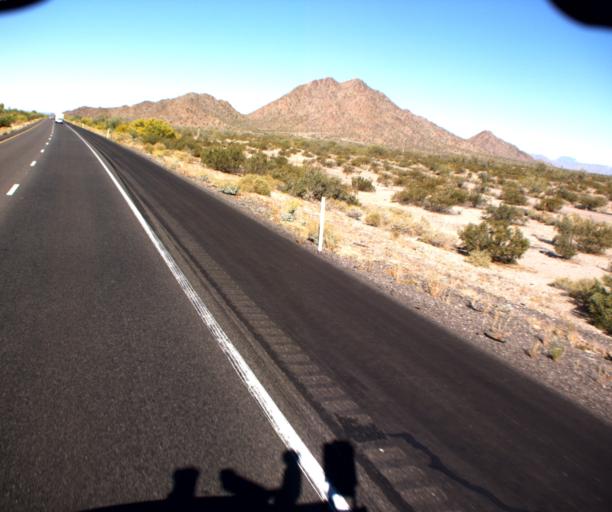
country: US
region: Arizona
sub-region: Maricopa County
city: Gila Bend
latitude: 32.9076
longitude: -112.5438
